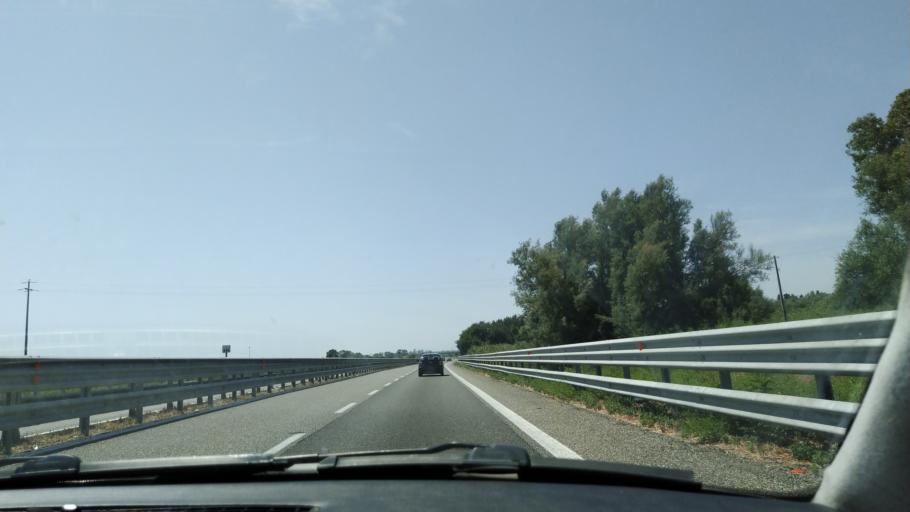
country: IT
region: Basilicate
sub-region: Provincia di Matera
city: Marconia
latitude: 40.3473
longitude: 16.7669
